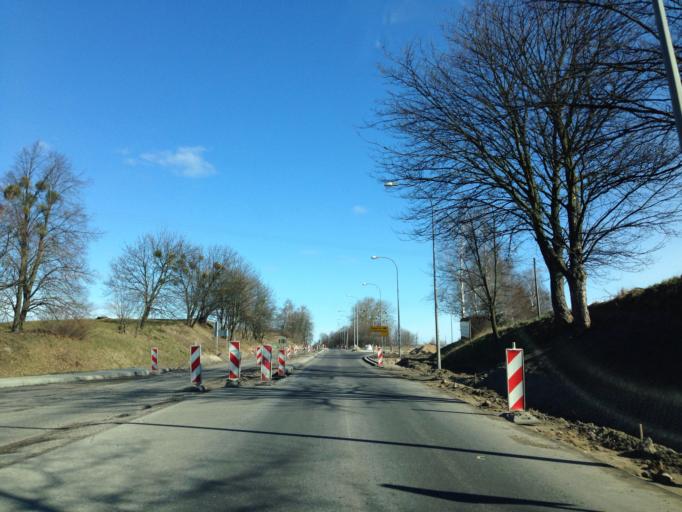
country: PL
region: Pomeranian Voivodeship
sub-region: Powiat tczewski
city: Tczew
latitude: 54.0600
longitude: 18.7674
